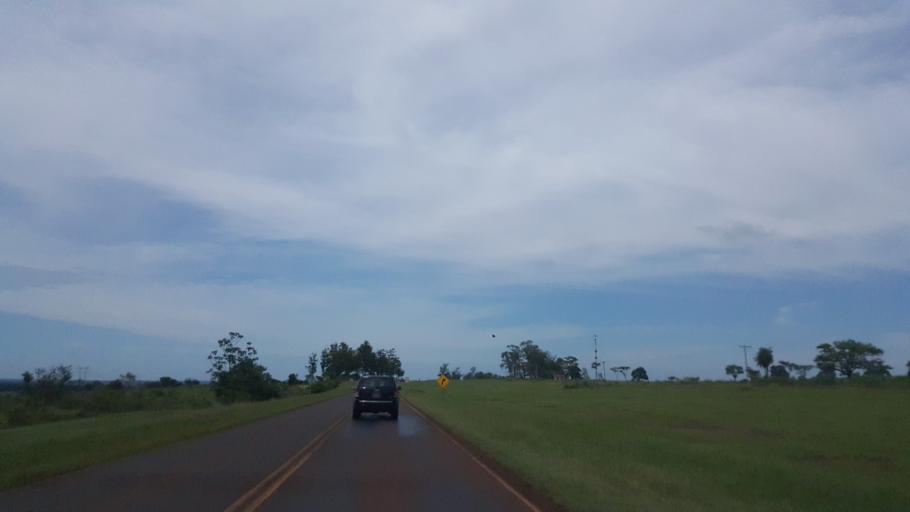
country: PY
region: Itapua
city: San Juan del Parana
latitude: -27.4931
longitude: -56.0955
